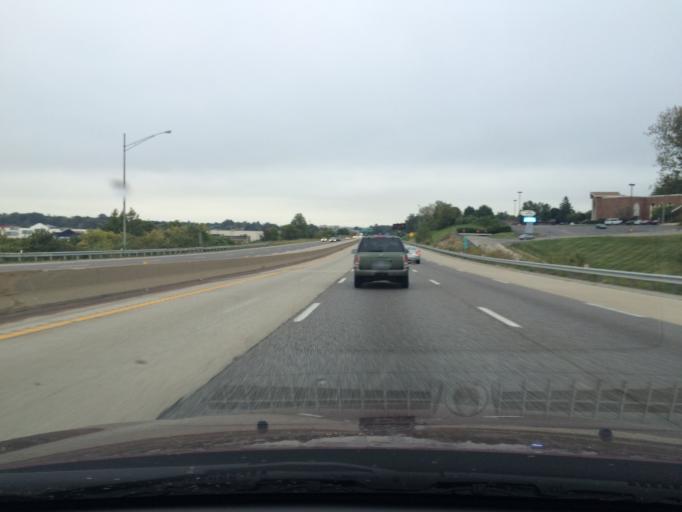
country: US
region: Missouri
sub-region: Saint Louis County
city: Bridgeton
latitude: 38.7455
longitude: -90.4299
